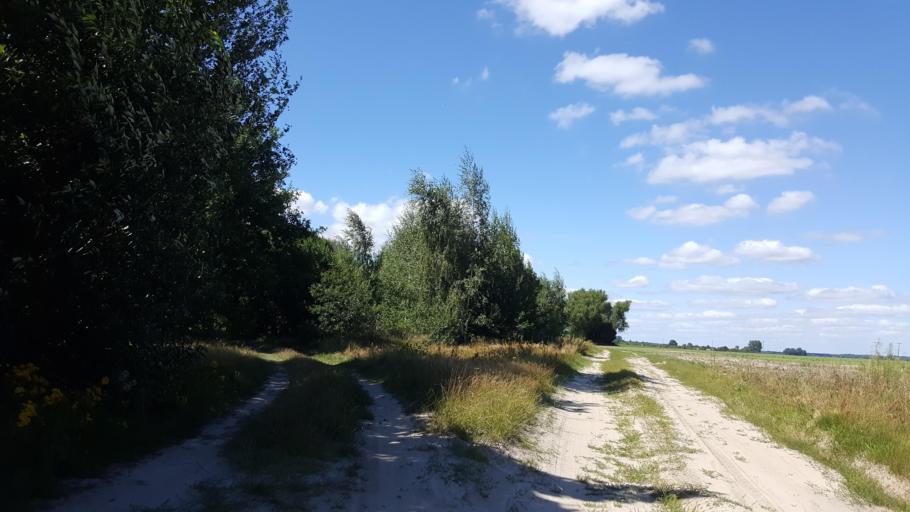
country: BY
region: Brest
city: Kobryn
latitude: 52.3068
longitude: 24.3140
